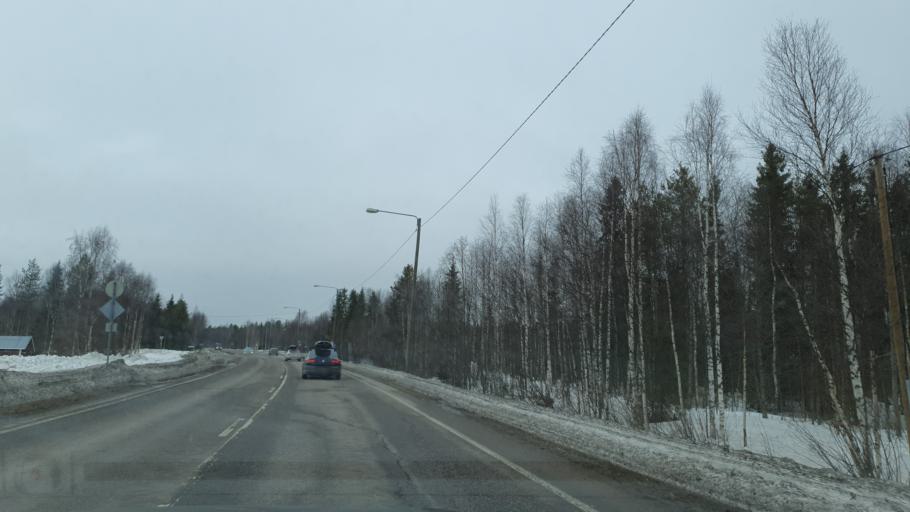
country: FI
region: Lapland
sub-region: Torniolaakso
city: Pello
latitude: 66.8226
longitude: 24.0034
